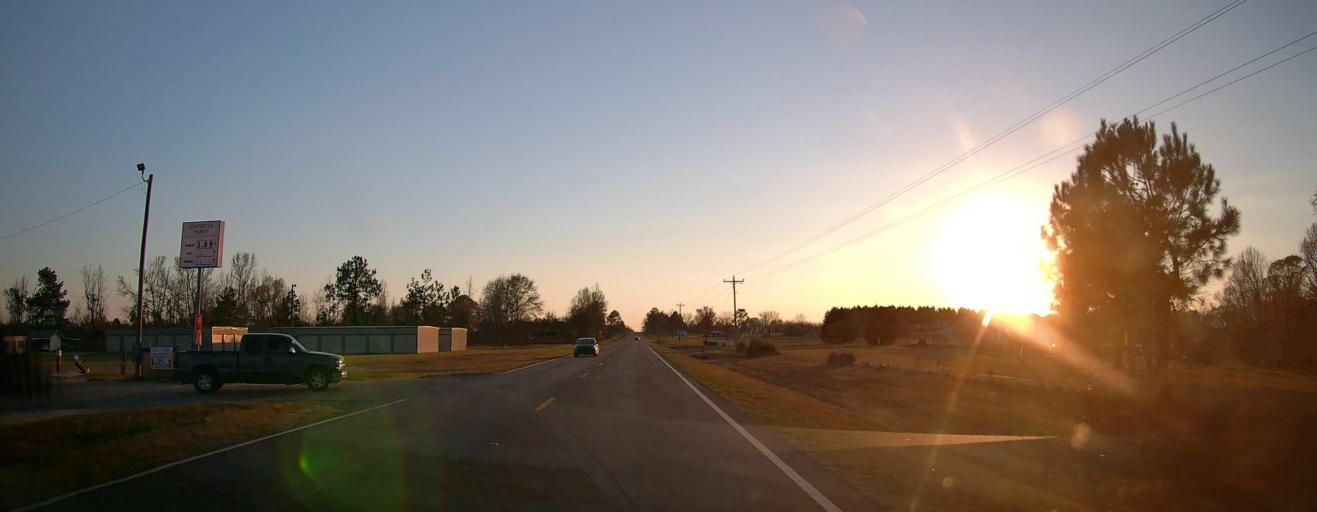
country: US
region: Georgia
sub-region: Dodge County
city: Chester
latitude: 32.3623
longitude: -83.0134
